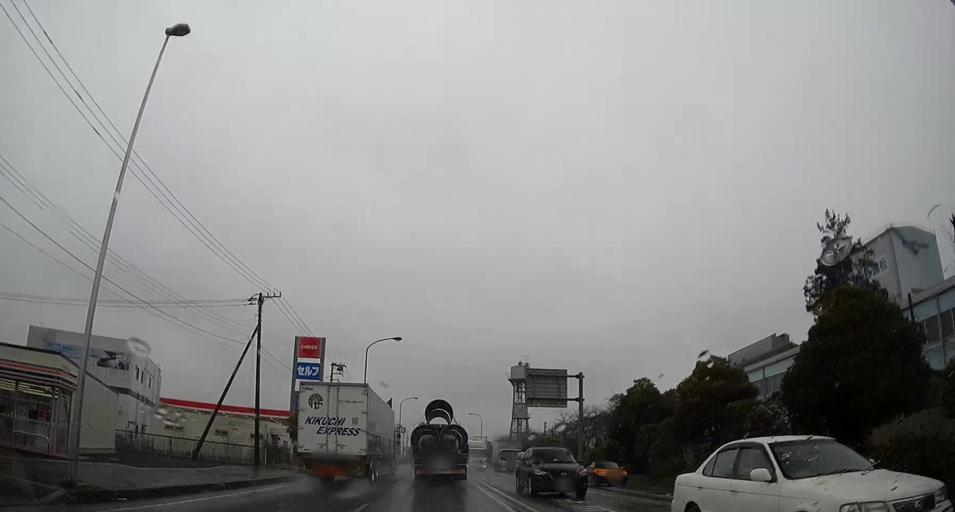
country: JP
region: Chiba
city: Chiba
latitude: 35.5628
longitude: 140.1287
